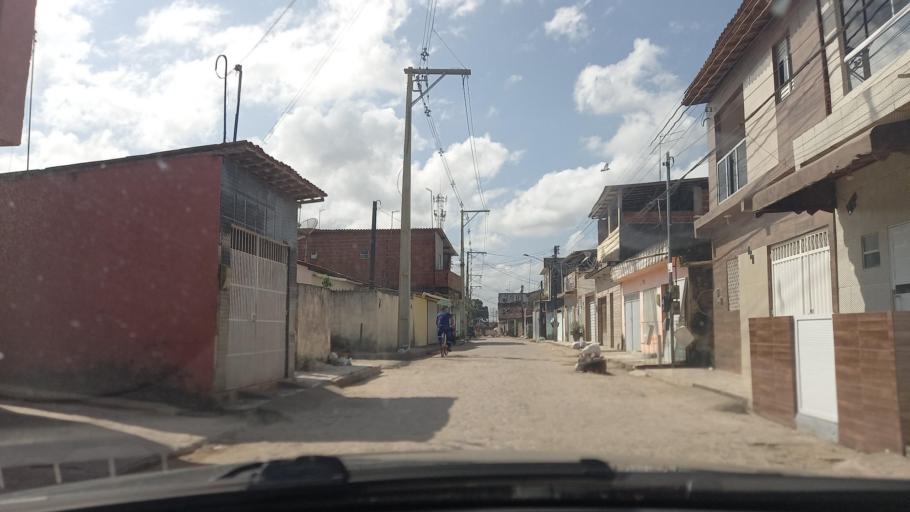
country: BR
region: Pernambuco
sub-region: Goiana
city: Goiana
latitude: -7.5659
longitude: -35.0135
